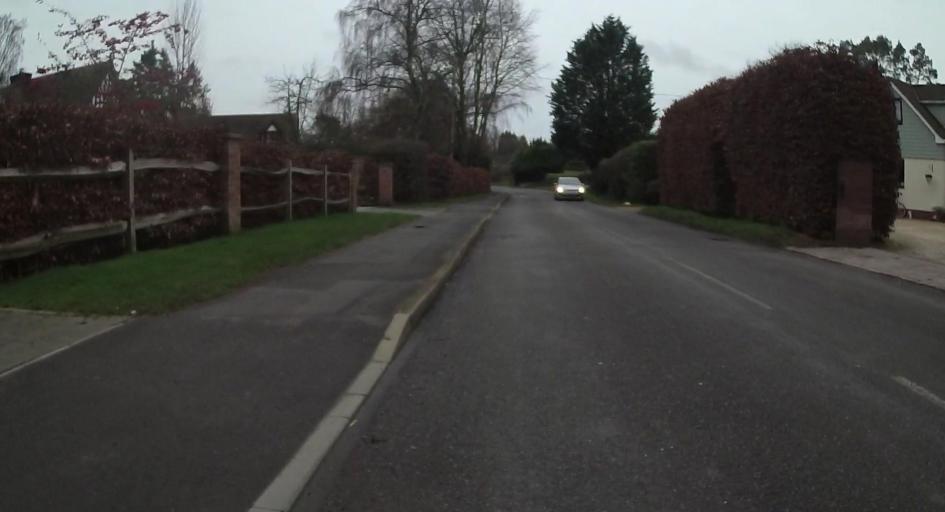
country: GB
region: England
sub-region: Hampshire
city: Four Marks
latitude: 51.1033
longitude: -1.0493
